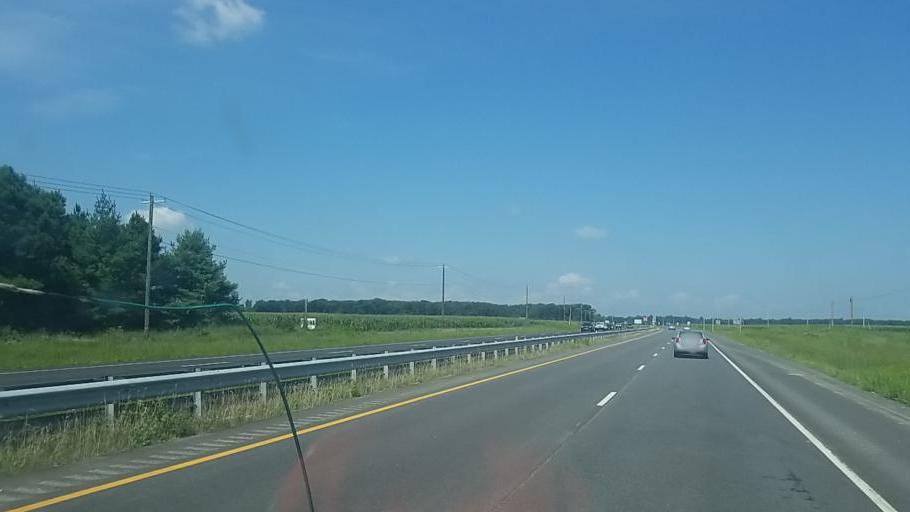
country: US
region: Maryland
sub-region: Caroline County
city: Ridgely
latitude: 38.9107
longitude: -75.8864
